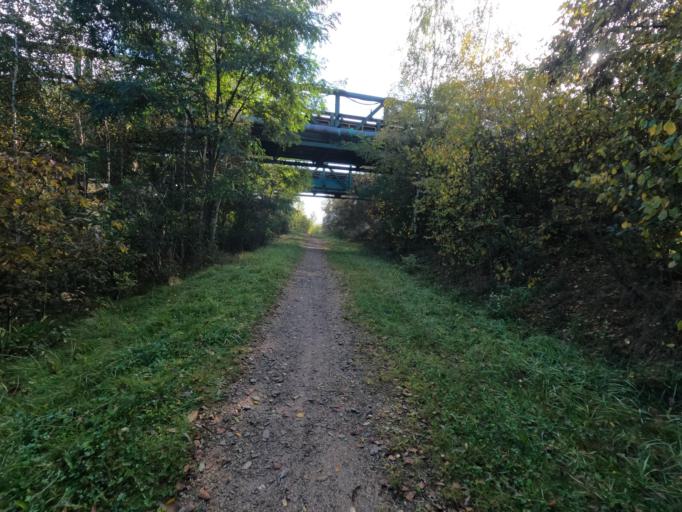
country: DE
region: North Rhine-Westphalia
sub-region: Regierungsbezirk Koln
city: Inden
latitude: 50.8569
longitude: 6.3232
